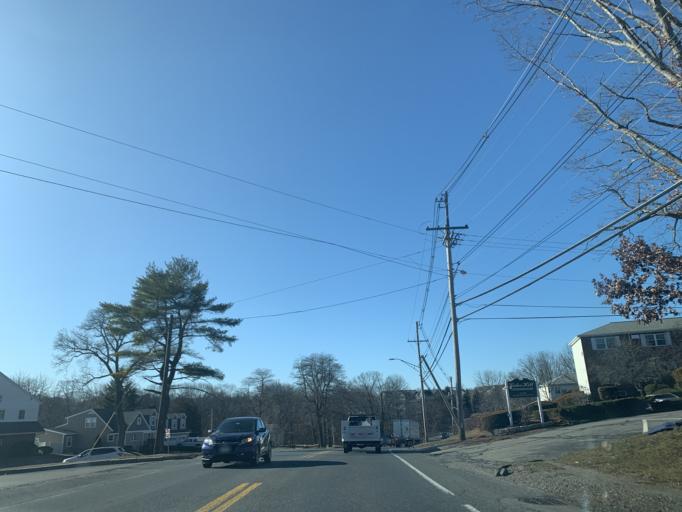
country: US
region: Massachusetts
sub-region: Middlesex County
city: Marlborough
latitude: 42.3491
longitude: -71.5237
